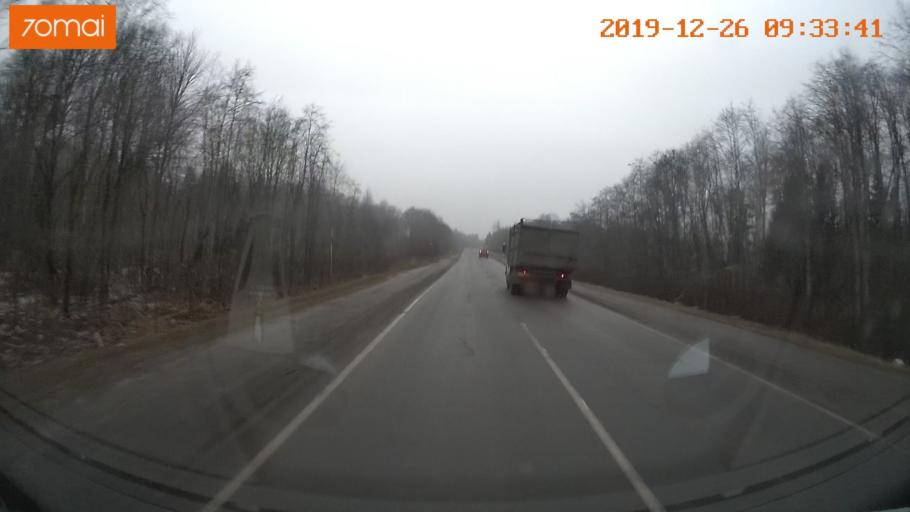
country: RU
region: Vologda
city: Vologda
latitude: 59.0927
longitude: 40.0967
